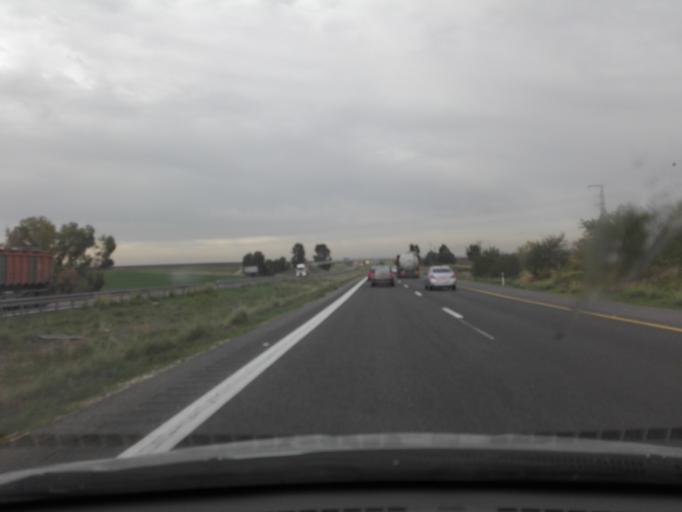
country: IL
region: Central District
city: Mazkeret Batya
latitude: 31.8369
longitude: 34.8590
